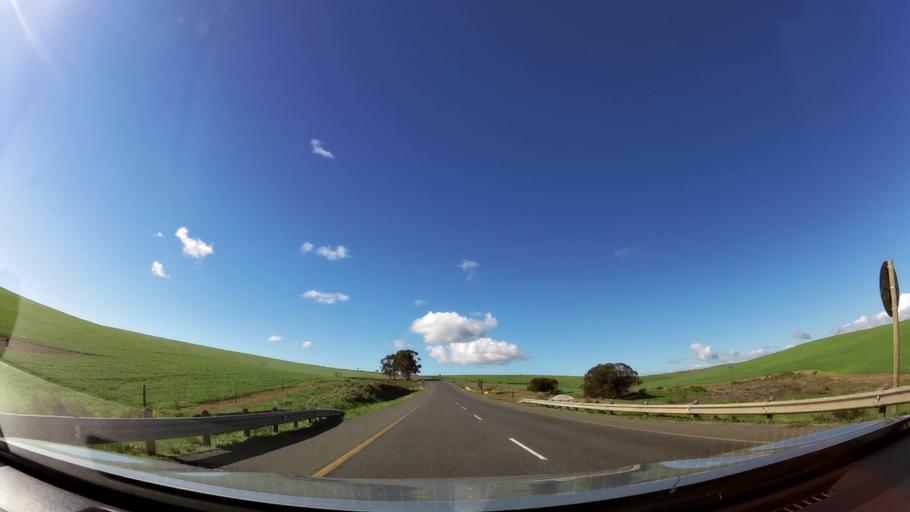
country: ZA
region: Western Cape
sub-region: Overberg District Municipality
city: Caledon
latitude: -34.1846
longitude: 19.6975
